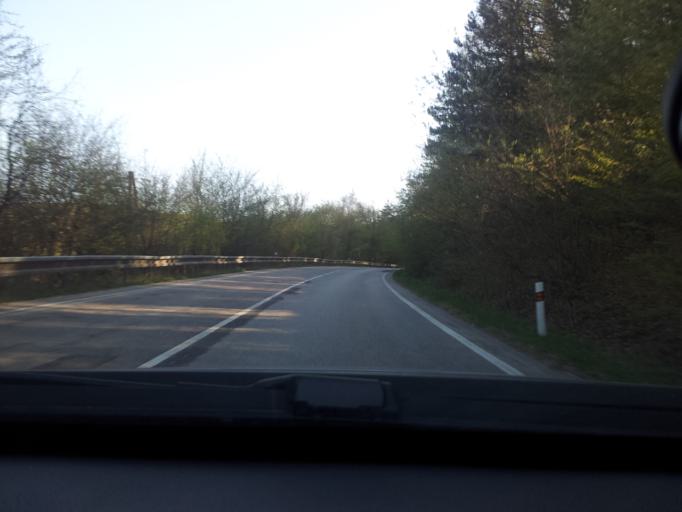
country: SK
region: Nitriansky
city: Zlate Moravce
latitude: 48.4883
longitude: 18.4201
